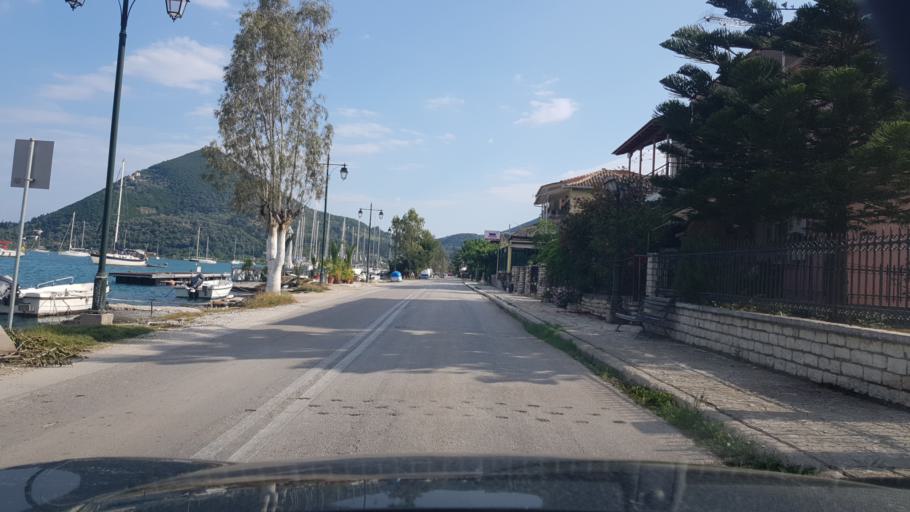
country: GR
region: Ionian Islands
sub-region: Lefkada
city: Nidri
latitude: 38.6883
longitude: 20.6987
